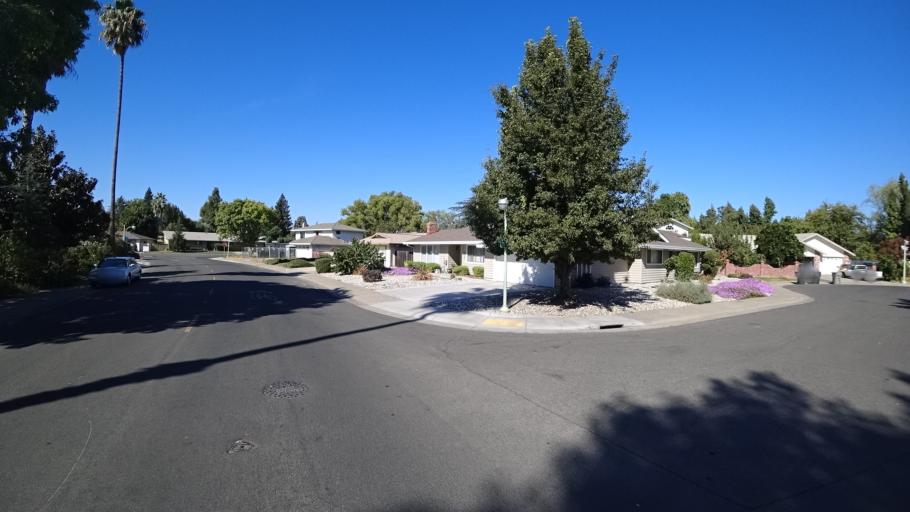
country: US
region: California
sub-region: Sacramento County
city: Parkway
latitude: 38.5042
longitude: -121.5202
